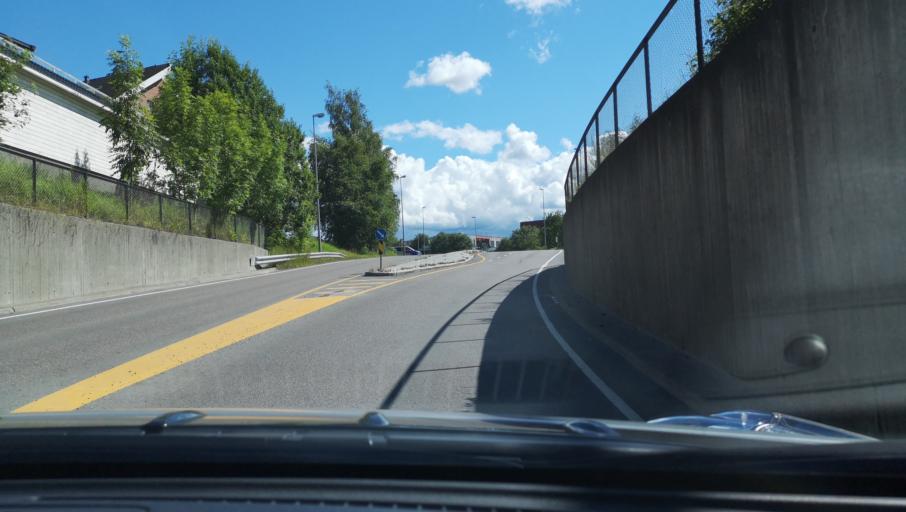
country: NO
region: Akershus
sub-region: As
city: As
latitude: 59.6657
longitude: 10.7941
